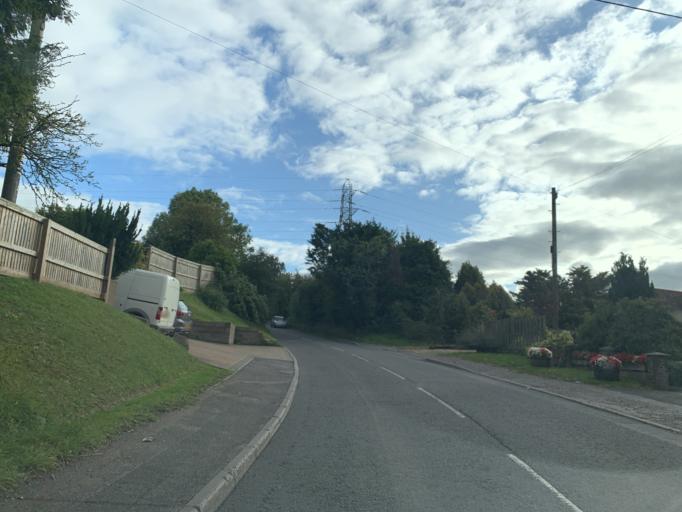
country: GB
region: England
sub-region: Wiltshire
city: Bulford
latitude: 51.1880
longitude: -1.7609
